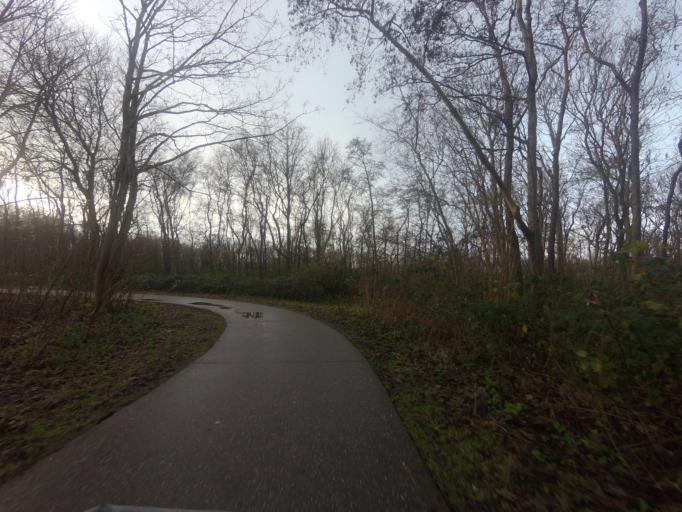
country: NL
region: North Holland
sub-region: Gemeente Texel
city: Den Burg
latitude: 53.1563
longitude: 4.8470
